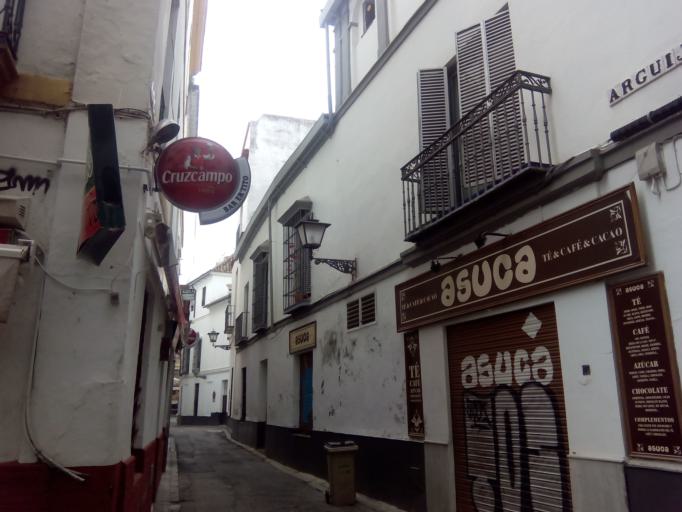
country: ES
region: Andalusia
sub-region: Provincia de Sevilla
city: Sevilla
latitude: 37.3939
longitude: -5.9929
